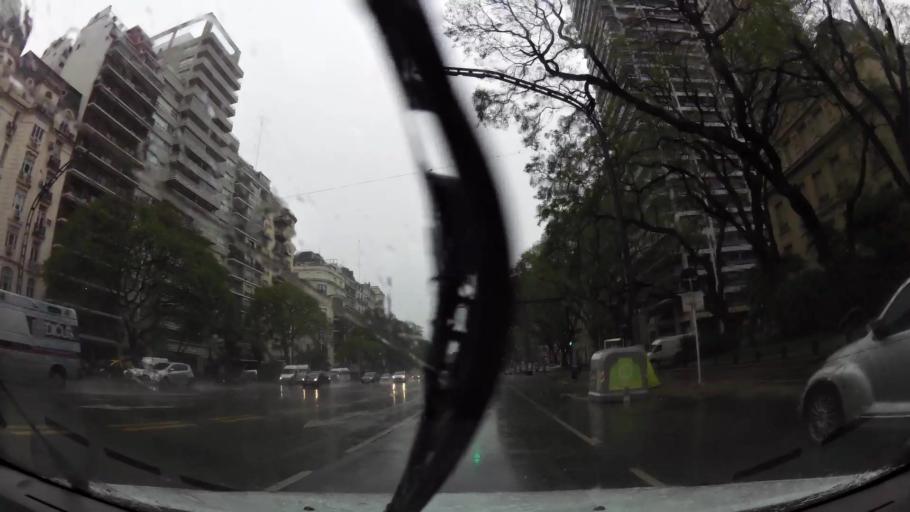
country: AR
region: Buenos Aires F.D.
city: Retiro
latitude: -34.5797
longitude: -58.4054
